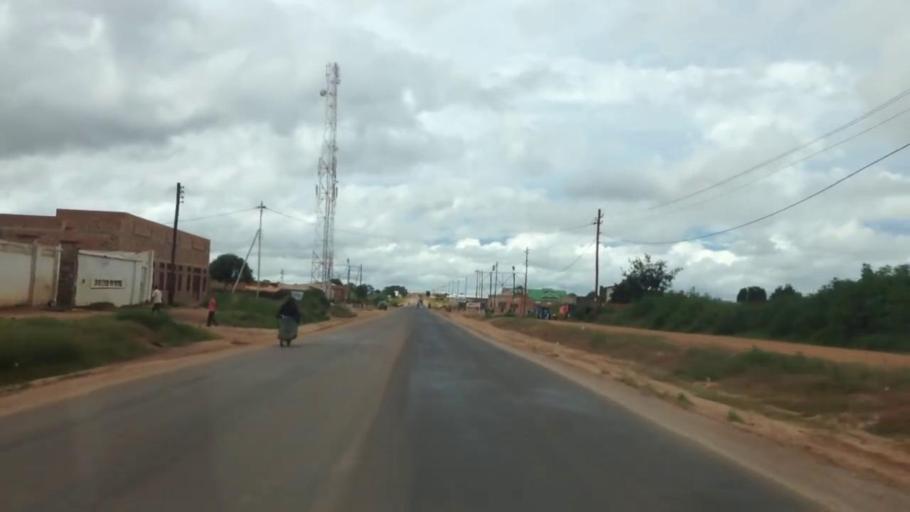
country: CD
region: Katanga
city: Kolwezi
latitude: -10.7333
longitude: 25.5104
